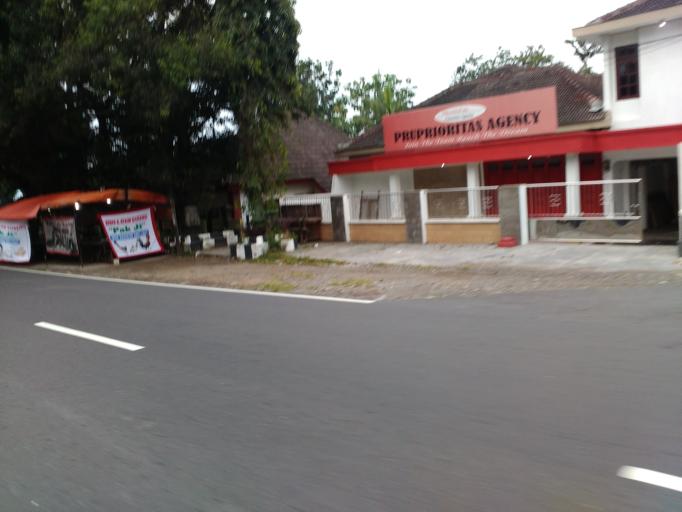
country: ID
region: Central Java
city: Boyolali
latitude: -7.5194
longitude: 110.5926
